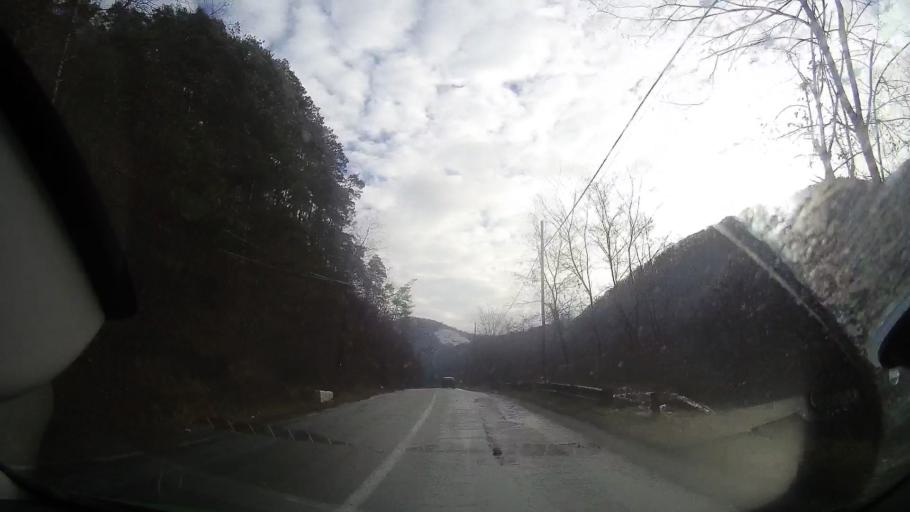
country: RO
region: Alba
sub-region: Oras Baia de Aries
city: Baia de Aries
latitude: 46.3757
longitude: 23.2504
